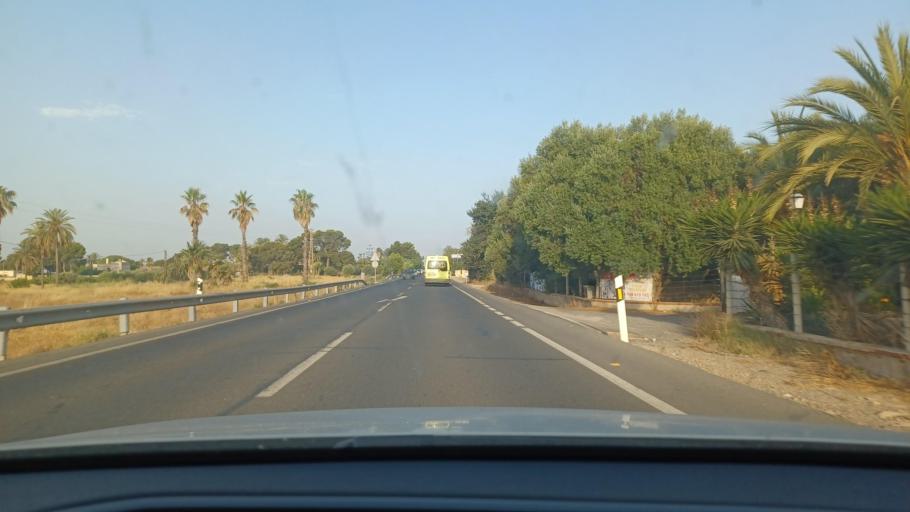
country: ES
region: Valencia
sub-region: Provincia de Alicante
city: Elche
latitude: 38.2789
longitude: -0.6455
